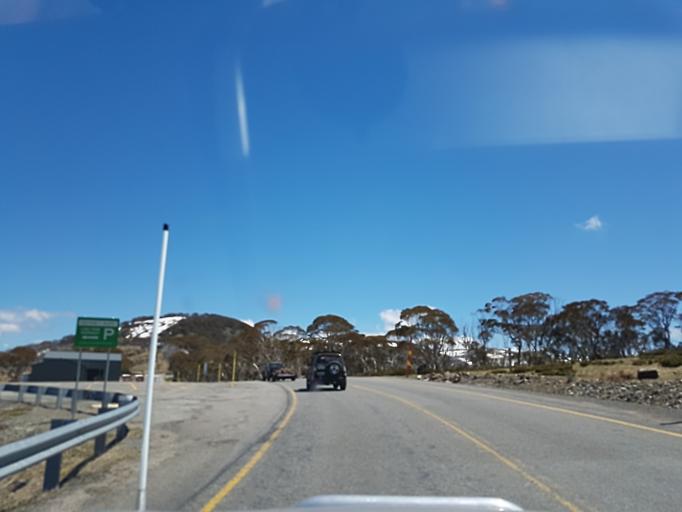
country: AU
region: Victoria
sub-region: Alpine
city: Mount Beauty
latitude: -36.9944
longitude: 147.1704
